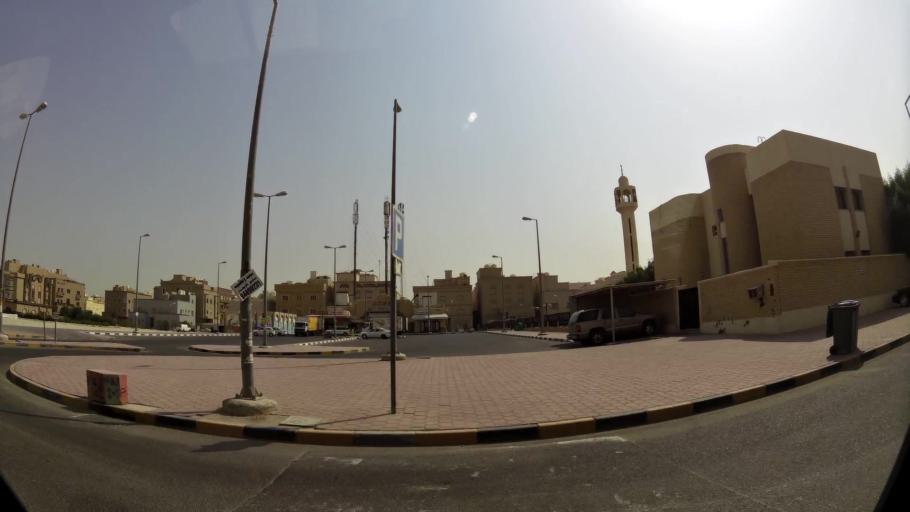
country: KW
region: Muhafazat al Jahra'
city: Al Jahra'
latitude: 29.3235
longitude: 47.7363
